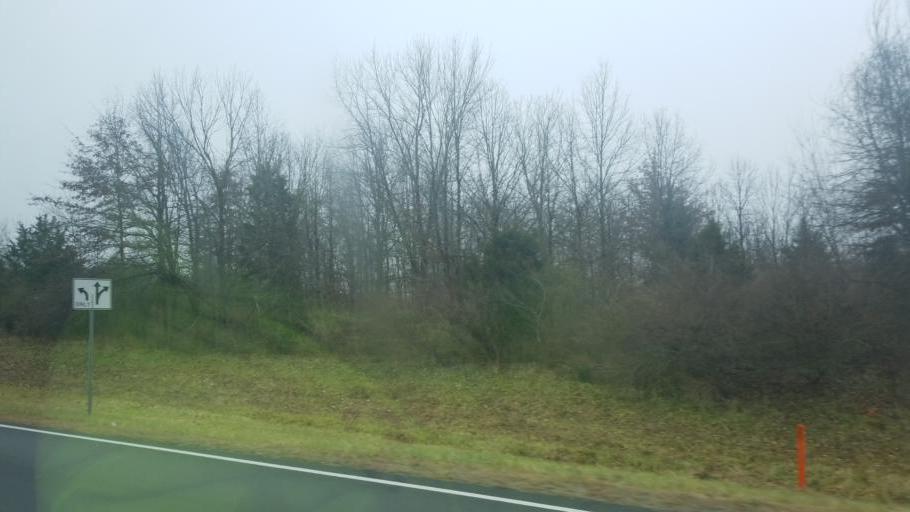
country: US
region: Ohio
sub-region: Champaign County
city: North Lewisburg
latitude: 40.2639
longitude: -83.4709
